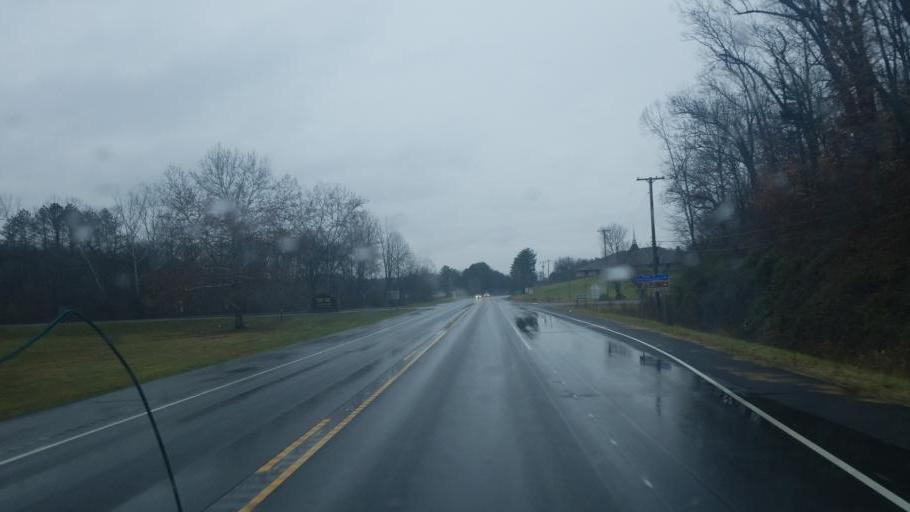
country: US
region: Indiana
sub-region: Brown County
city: Nashville
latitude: 39.1972
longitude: -86.2150
